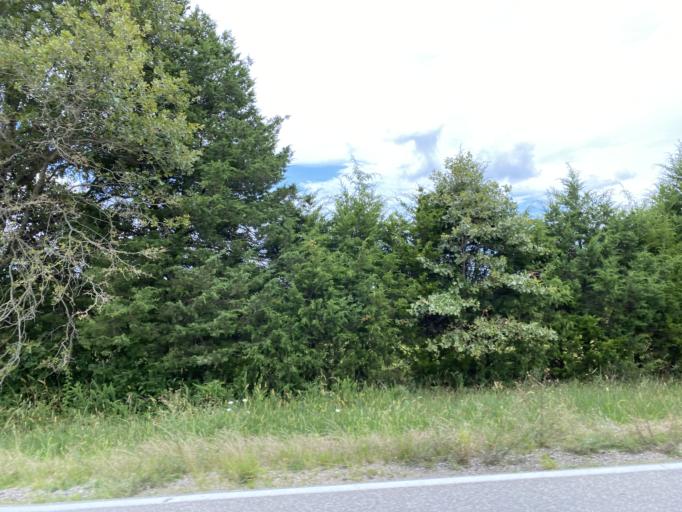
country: US
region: Arkansas
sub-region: Fulton County
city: Salem
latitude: 36.4272
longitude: -91.7067
